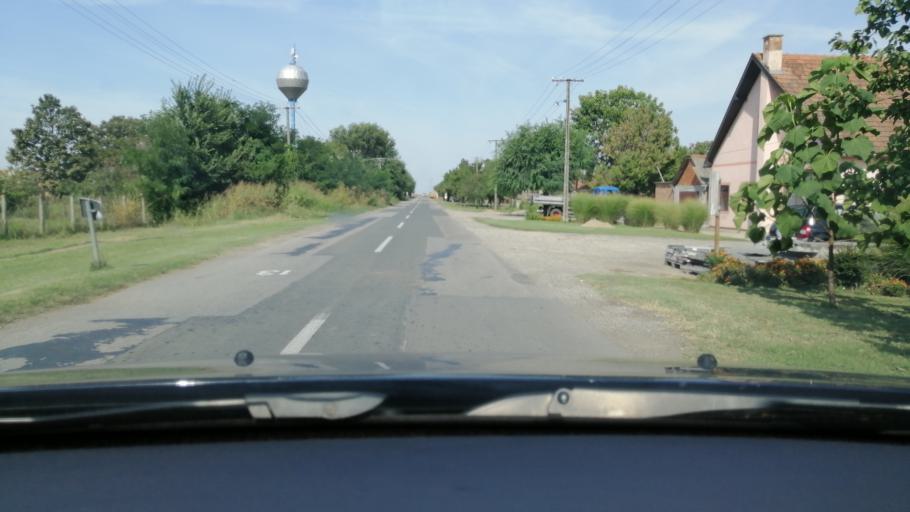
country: RS
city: Orlovat
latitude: 45.2489
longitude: 20.5806
